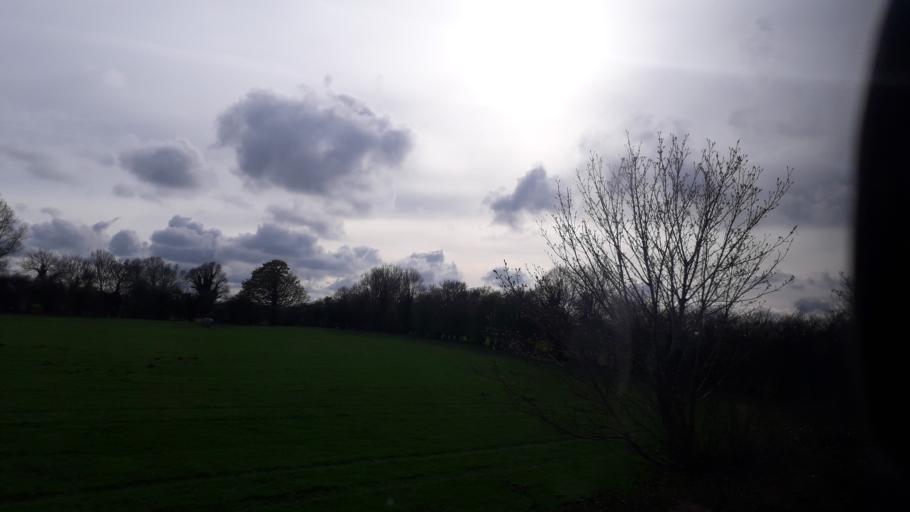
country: IE
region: Leinster
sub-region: An Mhi
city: Enfield
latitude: 53.4194
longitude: -6.8009
